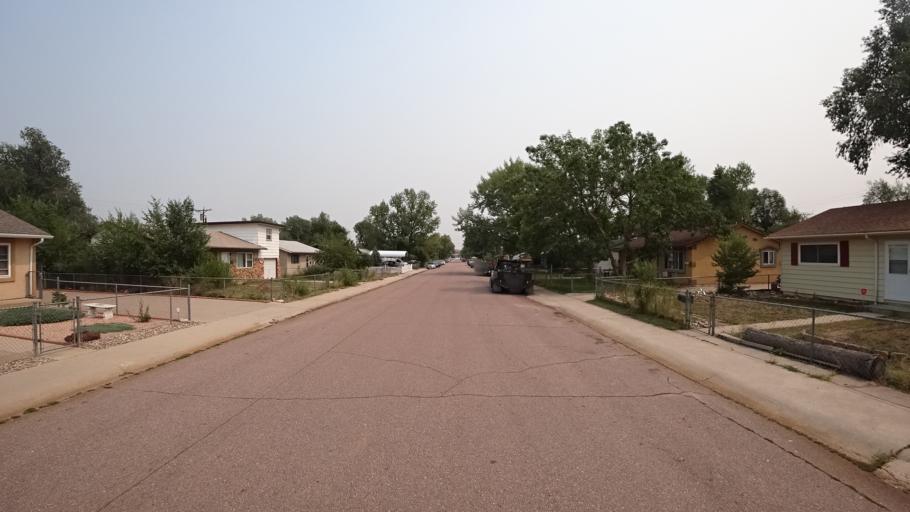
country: US
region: Colorado
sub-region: El Paso County
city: Stratmoor
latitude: 38.7975
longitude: -104.8058
